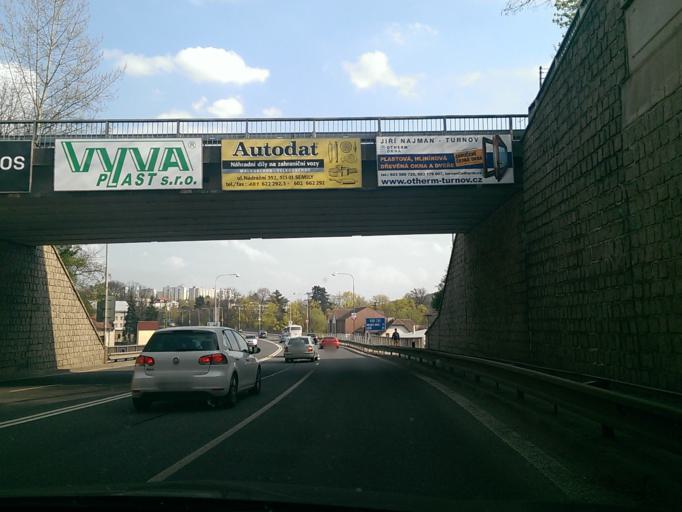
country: CZ
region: Liberecky
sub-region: Okres Semily
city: Turnov
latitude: 50.5866
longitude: 15.1454
